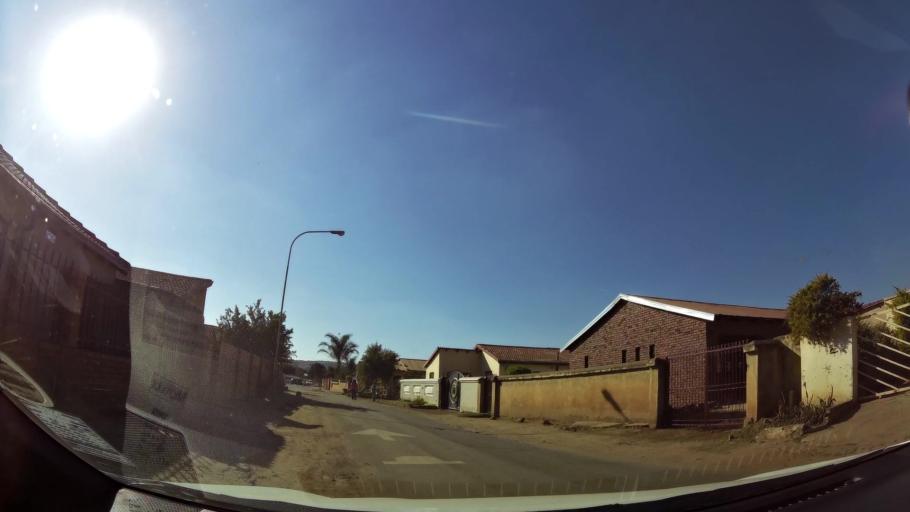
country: ZA
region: Gauteng
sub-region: City of Tshwane Metropolitan Municipality
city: Cullinan
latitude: -25.7220
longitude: 28.3795
